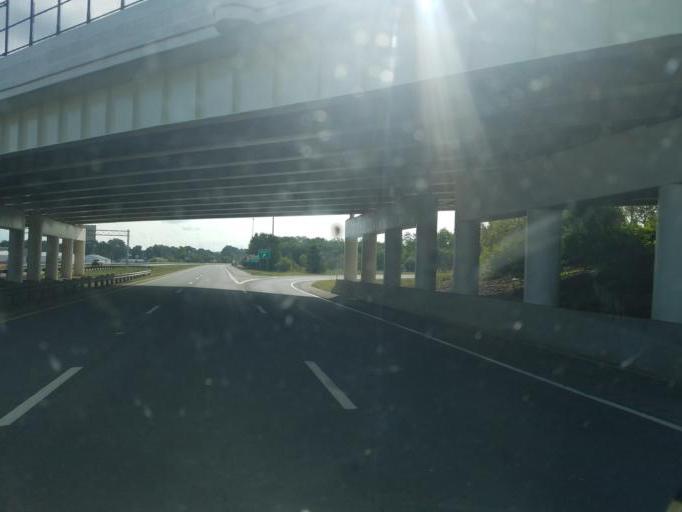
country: US
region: Ohio
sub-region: Wayne County
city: Wooster
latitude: 40.7913
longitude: -81.9514
